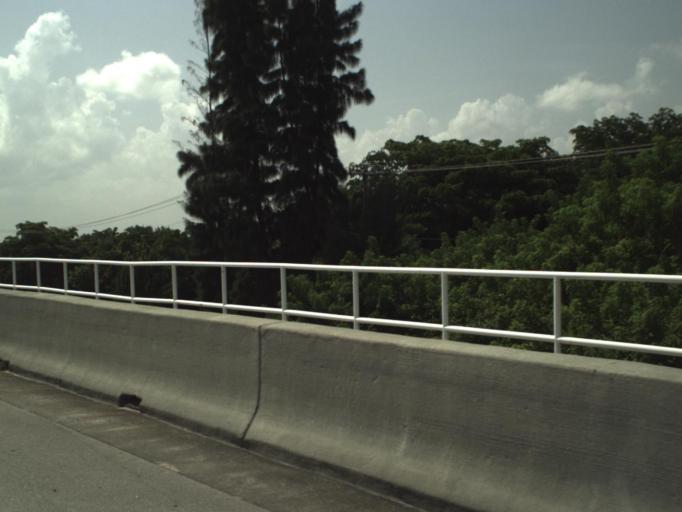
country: US
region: Florida
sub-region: Palm Beach County
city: Boca Pointe
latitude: 26.3178
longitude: -80.1691
